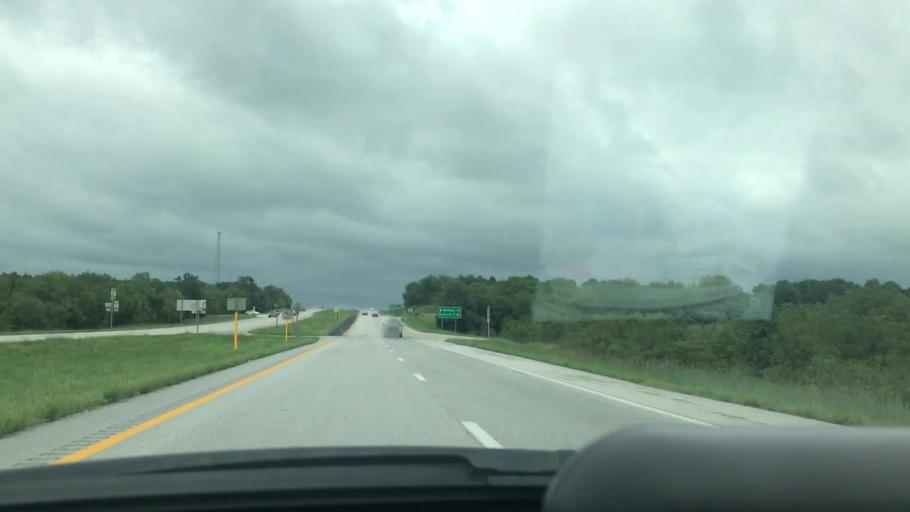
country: US
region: Missouri
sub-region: Greene County
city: Fair Grove
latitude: 37.4200
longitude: -93.1451
